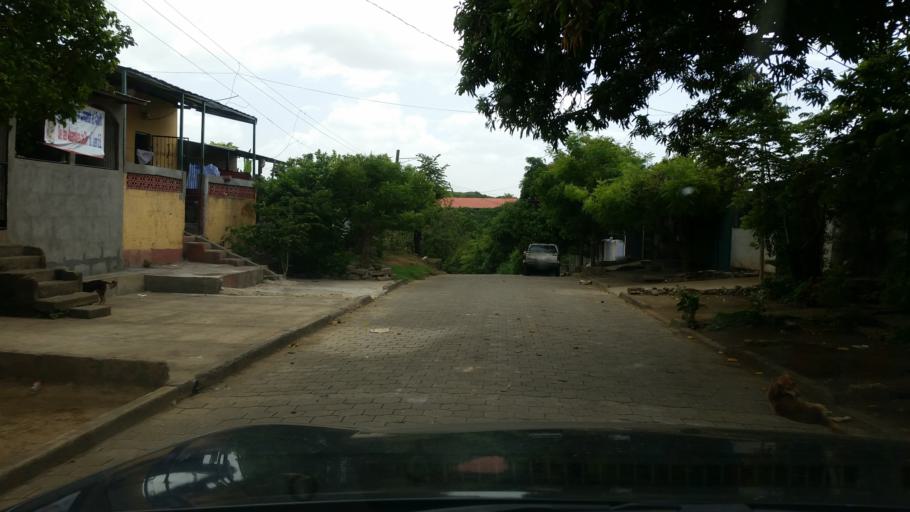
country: NI
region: Managua
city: Managua
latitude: 12.1041
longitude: -86.2248
